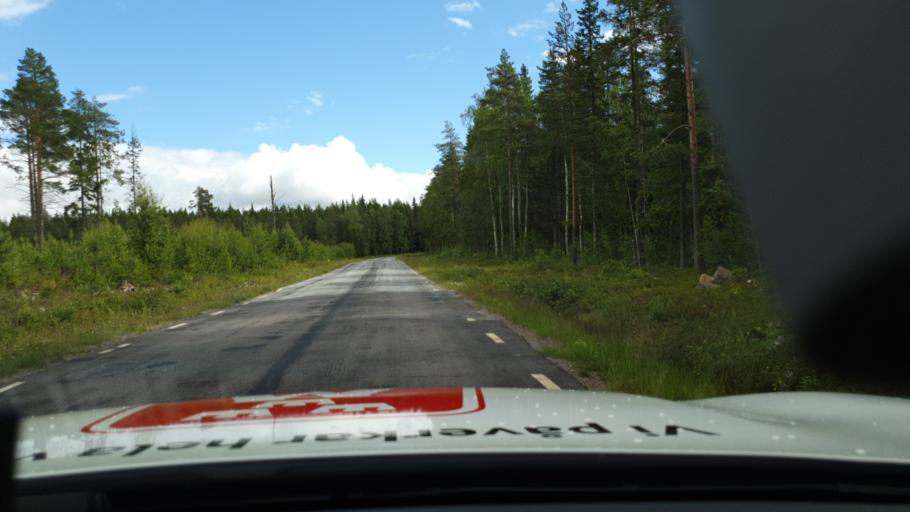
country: SE
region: Norrbotten
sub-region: Pitea Kommun
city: Rosvik
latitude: 65.4207
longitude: 21.8016
